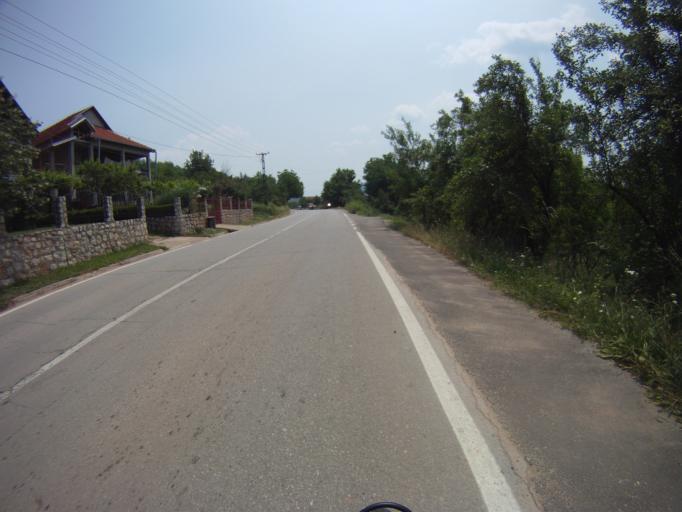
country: RS
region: Central Serbia
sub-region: Nisavski Okrug
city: Gadzin Han
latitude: 43.2370
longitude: 22.0208
